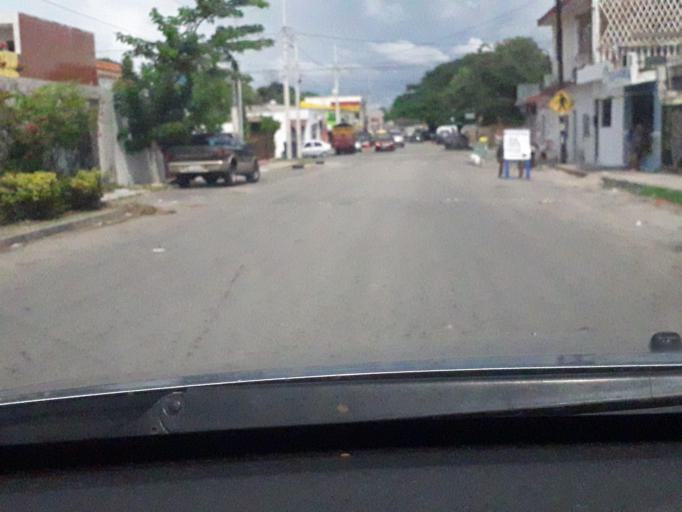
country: MX
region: Yucatan
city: Merida
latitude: 20.9689
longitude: -89.6589
